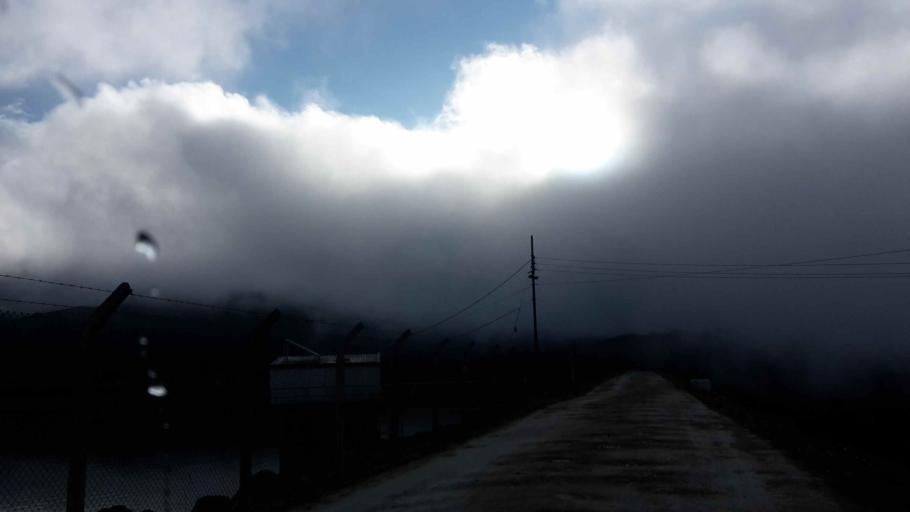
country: BO
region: Cochabamba
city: Colomi
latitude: -17.2272
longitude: -65.8913
